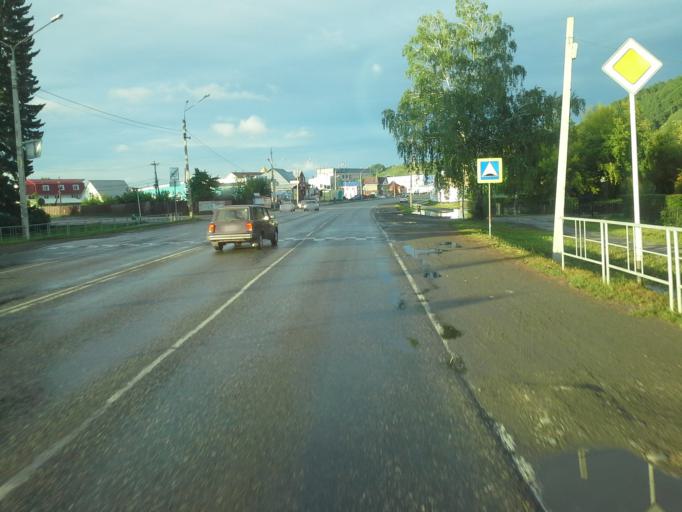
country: RU
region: Khabarovsk Krai
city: Mayma
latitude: 52.0024
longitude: 85.8972
